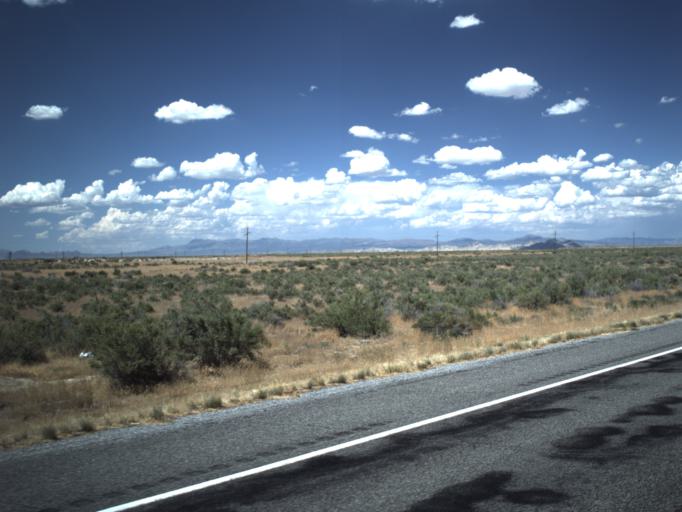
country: US
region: Utah
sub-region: Millard County
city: Delta
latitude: 39.4393
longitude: -112.4571
